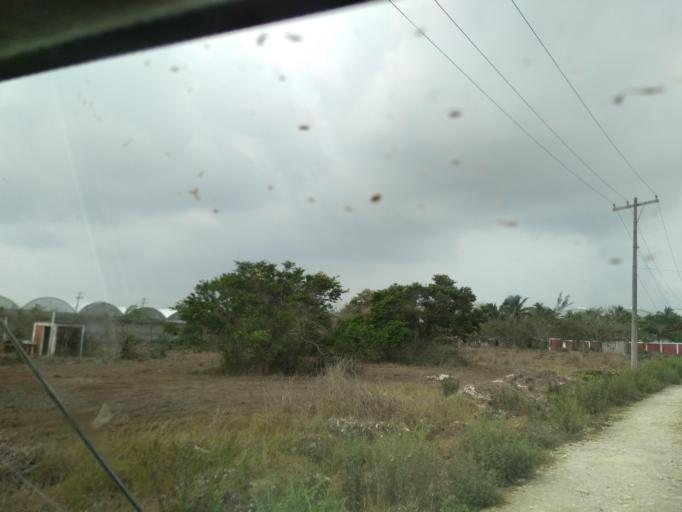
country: MX
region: Veracruz
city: Paso del Toro
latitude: 19.0116
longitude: -96.1149
